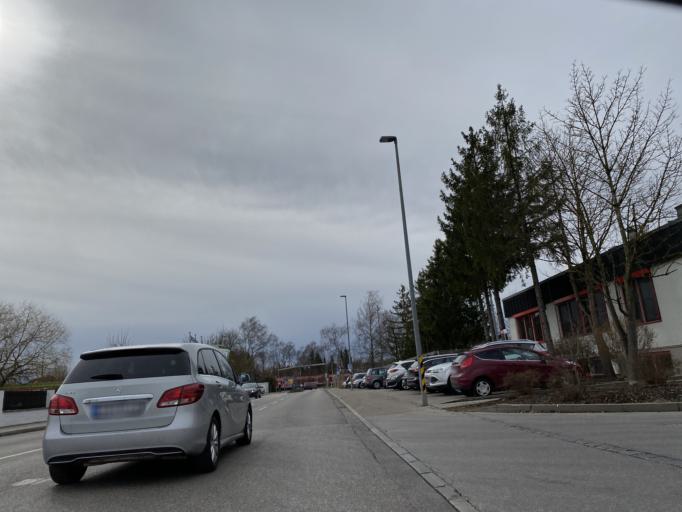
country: DE
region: Bavaria
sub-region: Upper Bavaria
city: Schongeising
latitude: 48.1604
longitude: 11.2217
